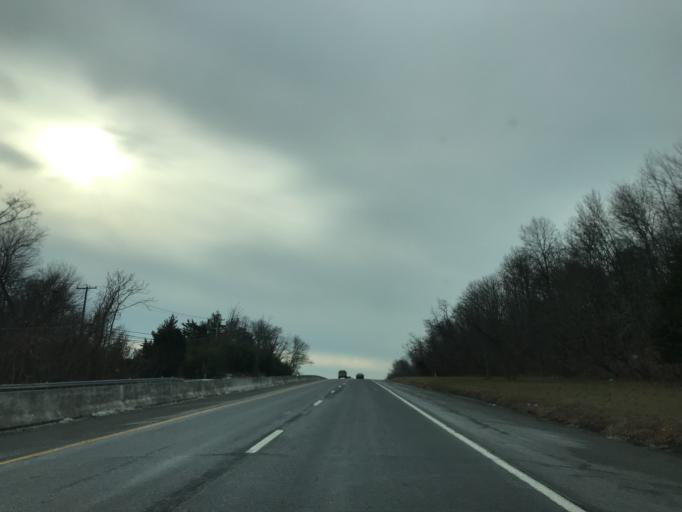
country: US
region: Maryland
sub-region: Harford County
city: Edgewood
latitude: 39.4489
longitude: -76.2809
